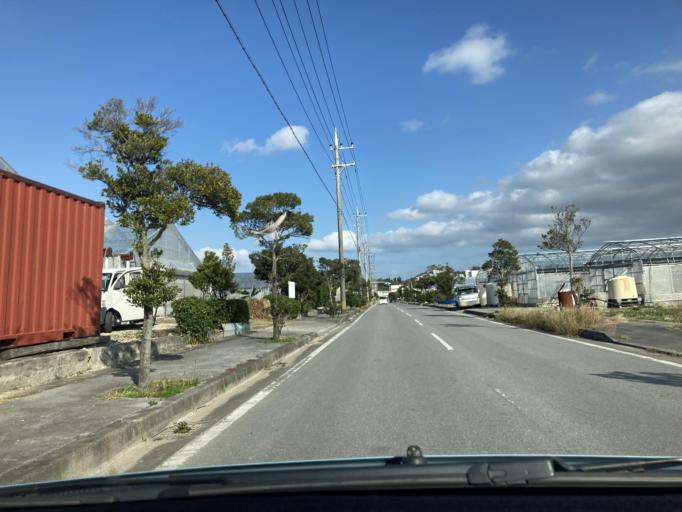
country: JP
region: Okinawa
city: Tomigusuku
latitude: 26.1702
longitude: 127.6624
